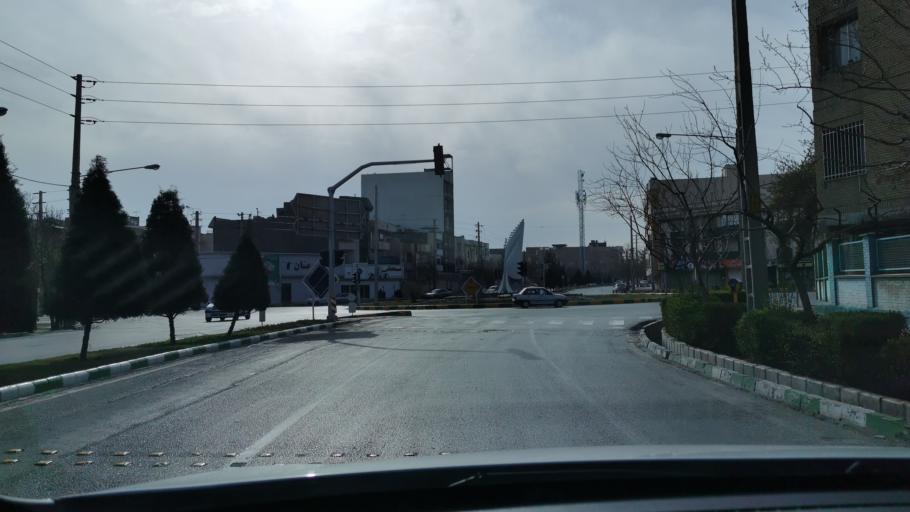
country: IR
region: Razavi Khorasan
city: Mashhad
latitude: 36.3132
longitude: 59.5145
